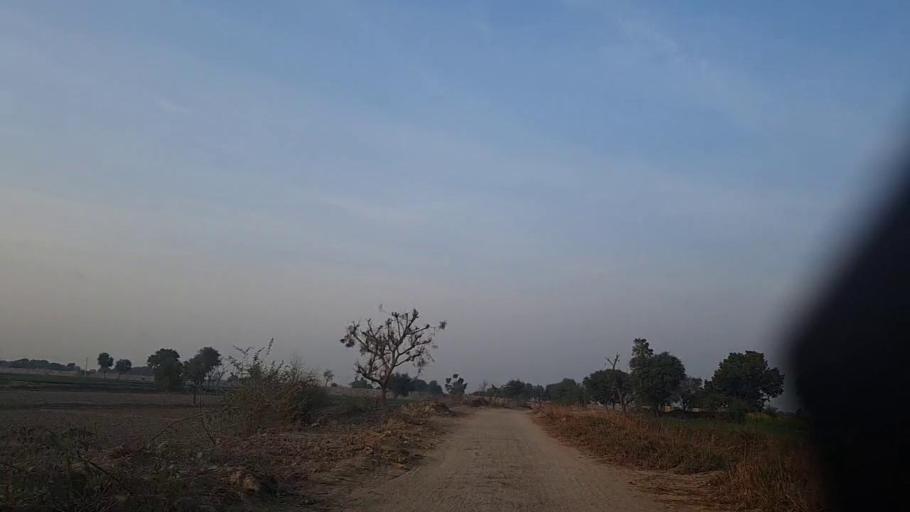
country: PK
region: Sindh
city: Sakrand
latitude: 26.1358
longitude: 68.2254
